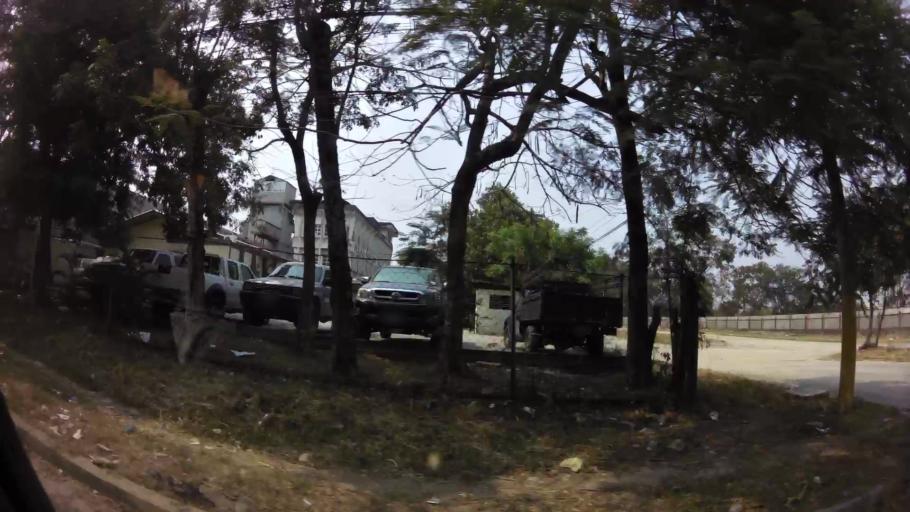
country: HN
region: Cortes
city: San Pedro Sula
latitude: 15.4880
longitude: -88.0254
